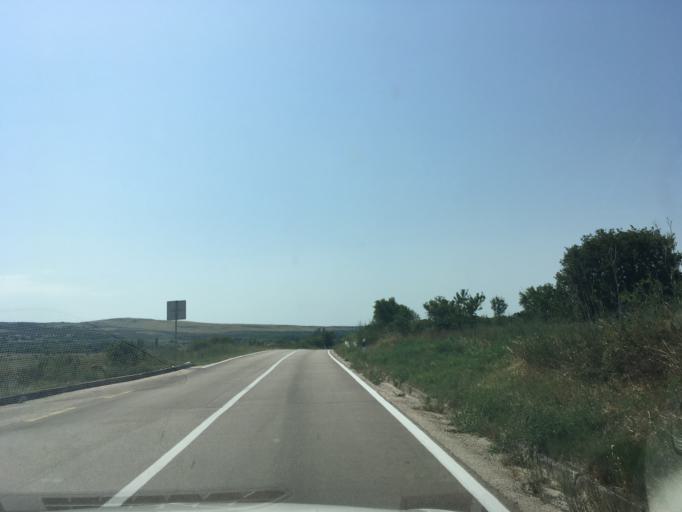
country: HR
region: Zadarska
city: Benkovac
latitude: 43.9670
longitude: 15.7239
